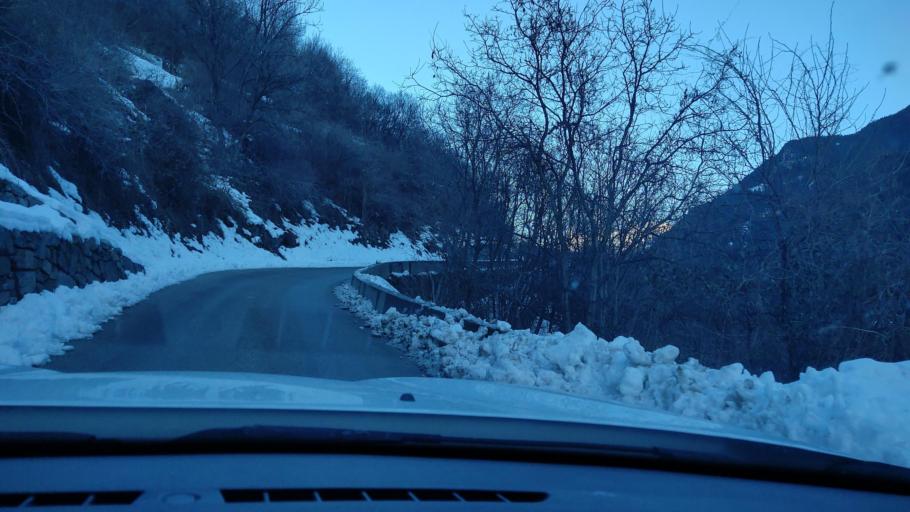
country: FR
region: Rhone-Alpes
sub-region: Departement de la Savoie
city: Saint-Michel-de-Maurienne
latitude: 45.2099
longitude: 6.5261
